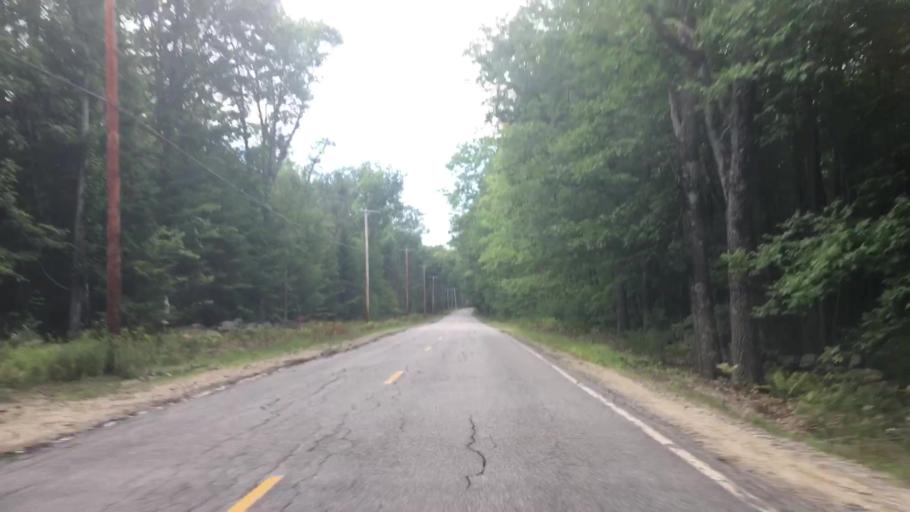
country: US
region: Maine
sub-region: Oxford County
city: Oxford
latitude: 44.0358
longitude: -70.5359
